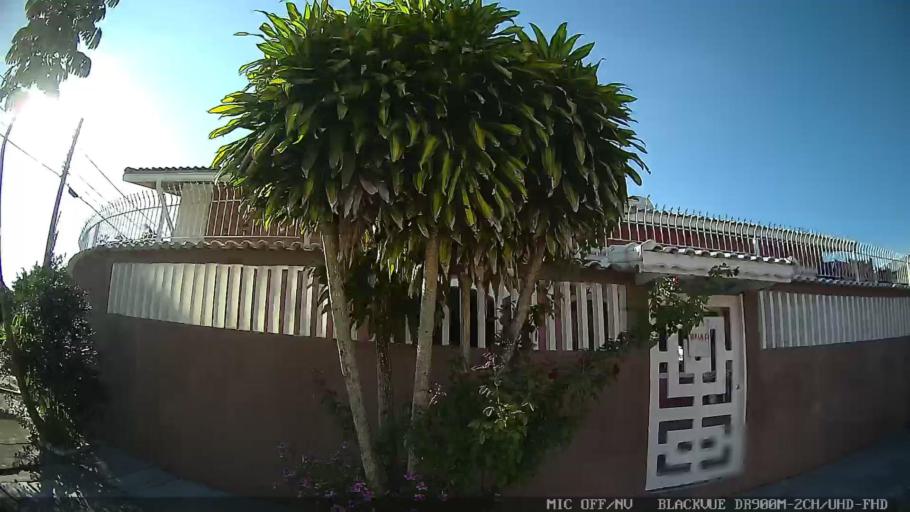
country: BR
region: Sao Paulo
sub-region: Peruibe
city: Peruibe
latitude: -24.3040
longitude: -46.9805
